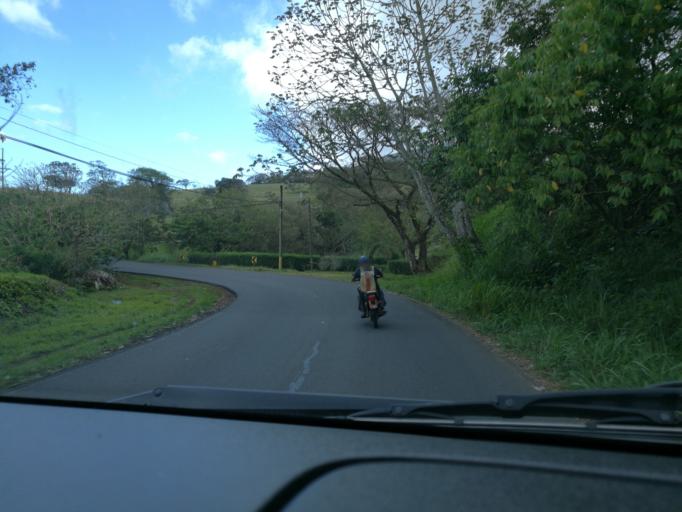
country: CR
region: Alajuela
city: Bijagua
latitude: 10.6745
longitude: -85.0908
